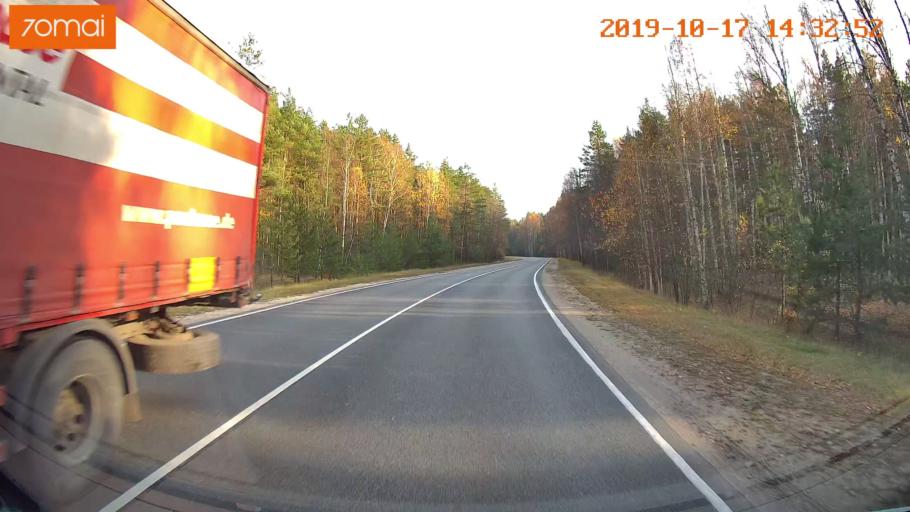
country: RU
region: Rjazan
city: Solotcha
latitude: 54.9267
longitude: 39.9875
